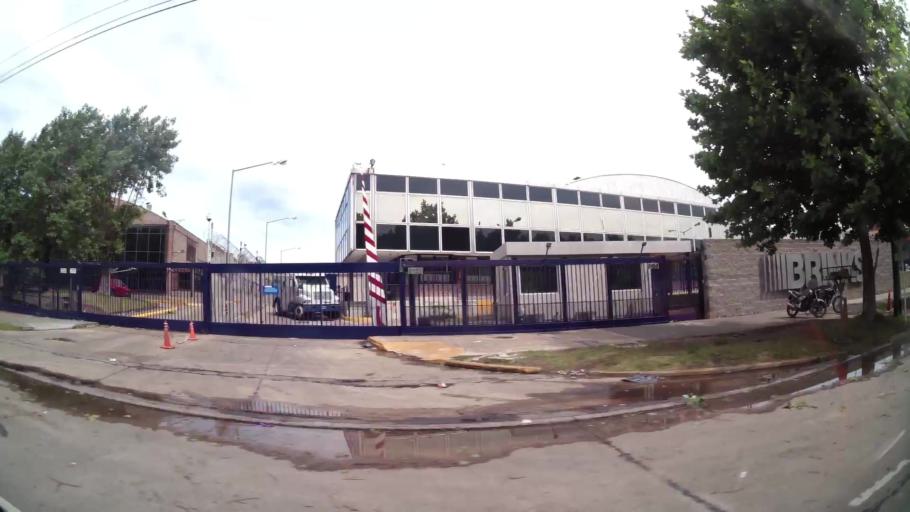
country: AR
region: Buenos Aires F.D.
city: Villa Lugano
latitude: -34.6649
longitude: -58.4373
